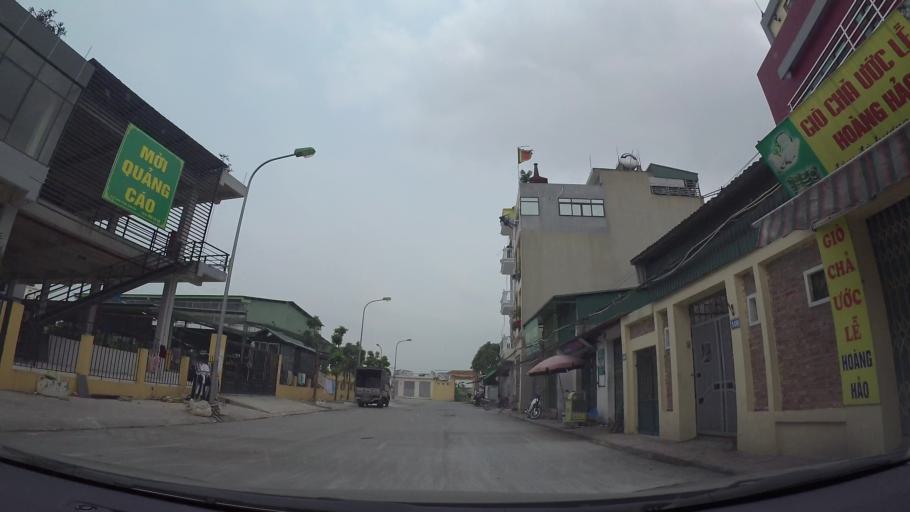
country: VN
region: Ha Noi
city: Trau Quy
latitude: 21.0569
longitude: 105.9016
